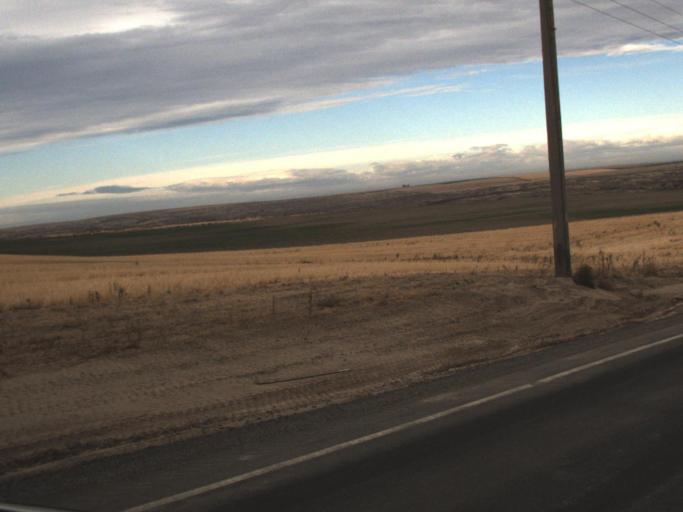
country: US
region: Washington
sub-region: Adams County
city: Ritzville
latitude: 47.4557
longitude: -118.7515
